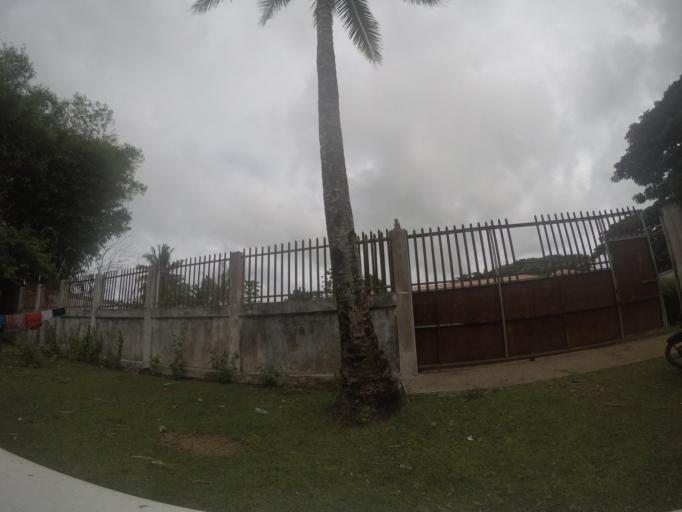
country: TL
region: Lautem
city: Lospalos
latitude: -8.5124
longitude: 126.9849
